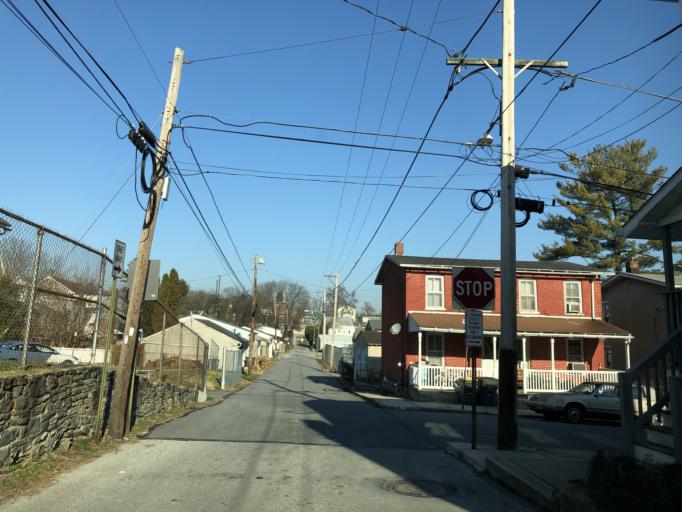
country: US
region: Pennsylvania
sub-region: Chester County
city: Downingtown
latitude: 39.9999
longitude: -75.7094
